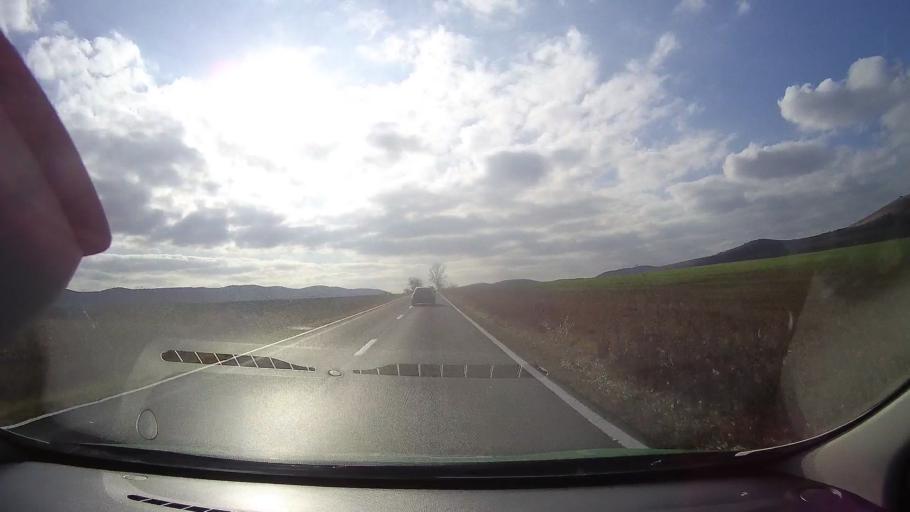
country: RO
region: Tulcea
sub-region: Comuna Nalbant
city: Nicolae Balcescu
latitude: 44.9873
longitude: 28.5572
